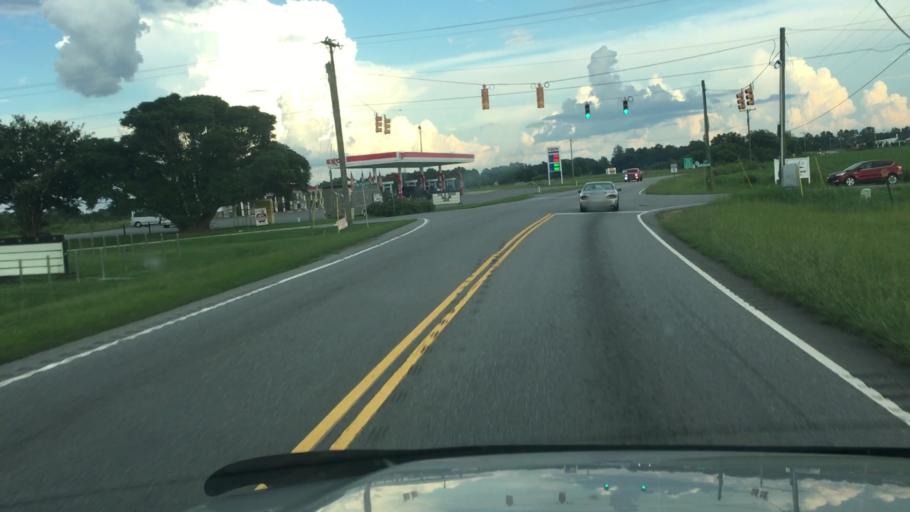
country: US
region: South Carolina
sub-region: Cherokee County
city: Gaffney
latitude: 35.1119
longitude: -81.7009
